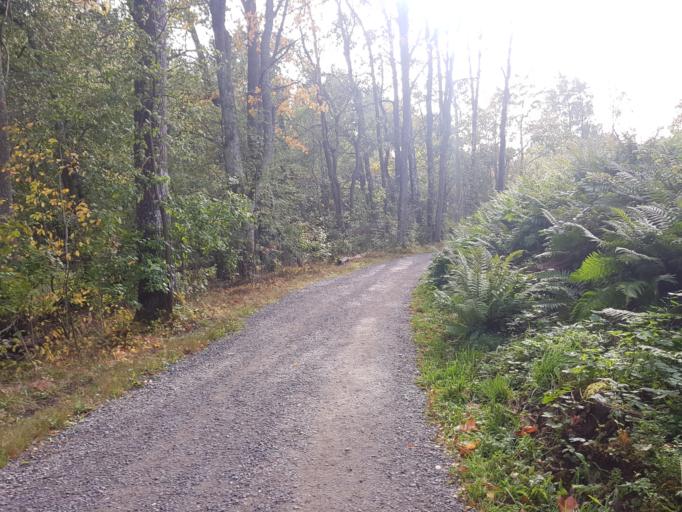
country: FI
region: Uusimaa
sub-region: Helsinki
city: Helsinki
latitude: 60.1384
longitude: 24.9962
